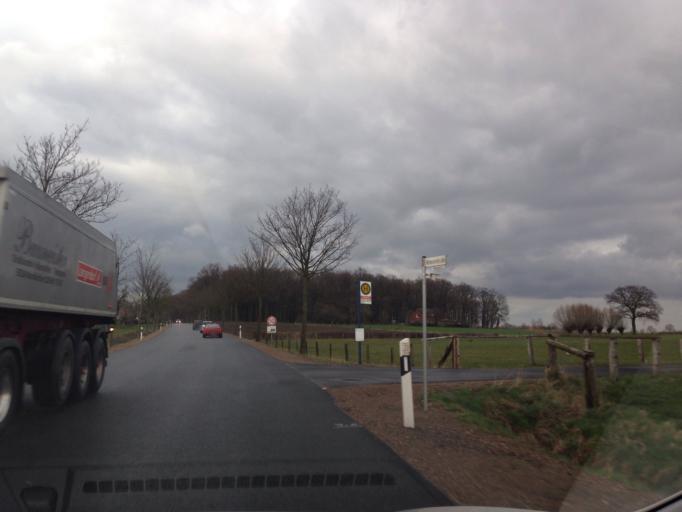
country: DE
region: North Rhine-Westphalia
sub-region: Regierungsbezirk Munster
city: Nordkirchen
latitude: 51.7725
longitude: 7.5447
